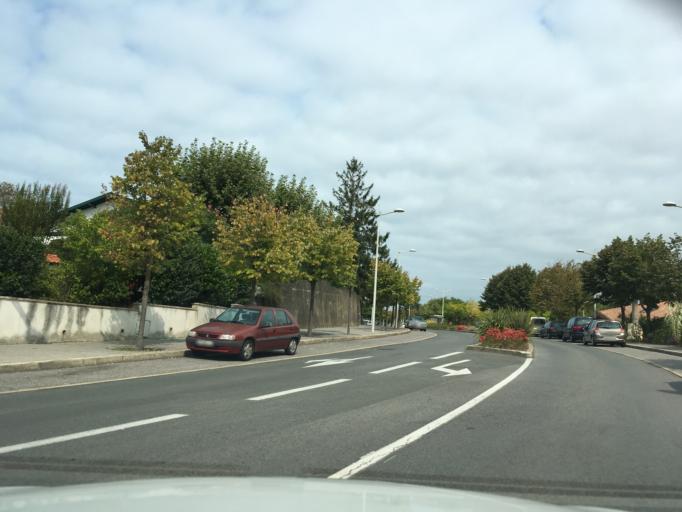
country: FR
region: Aquitaine
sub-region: Departement des Pyrenees-Atlantiques
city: Anglet
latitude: 43.4842
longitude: -1.5136
